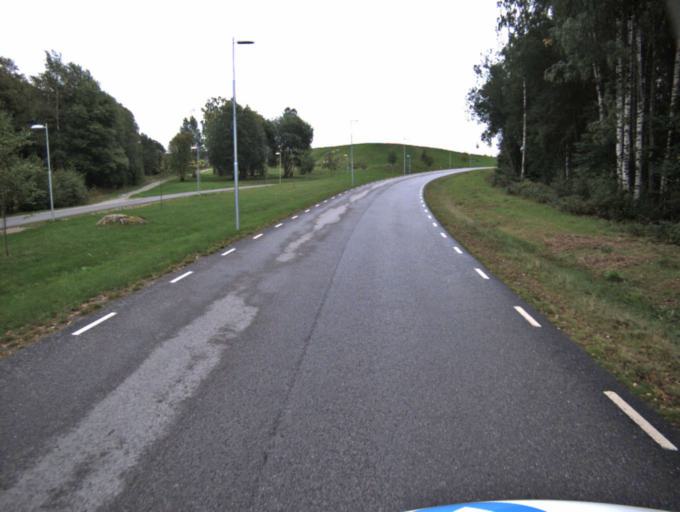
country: SE
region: Vaestra Goetaland
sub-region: Ulricehamns Kommun
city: Ulricehamn
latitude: 57.7877
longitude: 13.4306
